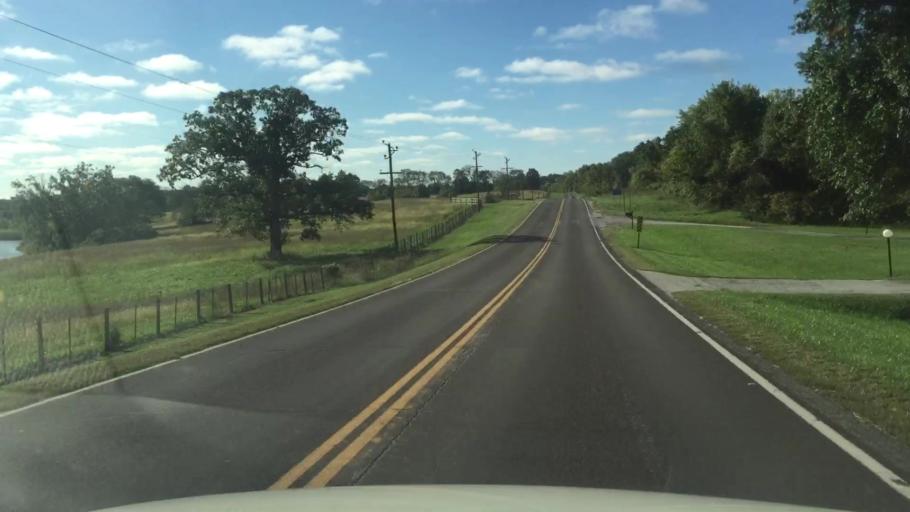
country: US
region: Missouri
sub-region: Howard County
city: New Franklin
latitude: 39.0446
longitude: -92.7444
